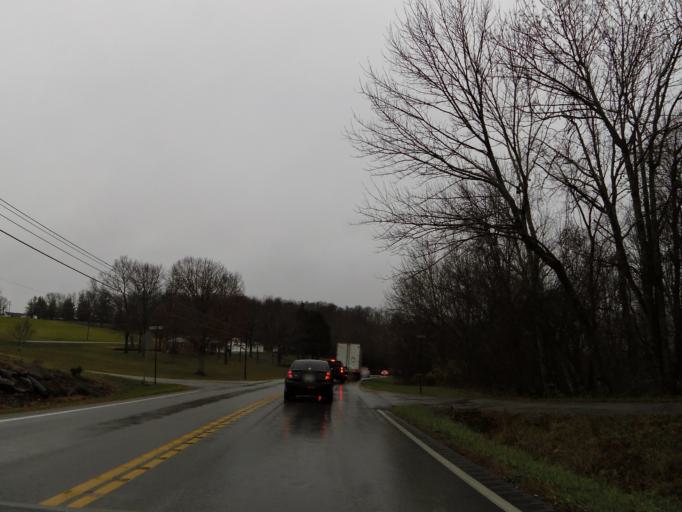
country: US
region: Kentucky
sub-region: Rockcastle County
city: Mount Vernon
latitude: 37.4161
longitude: -84.3333
